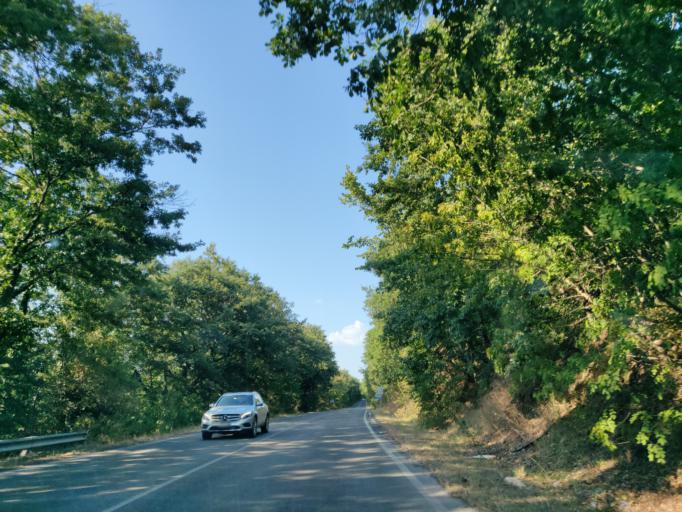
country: IT
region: Latium
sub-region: Provincia di Viterbo
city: Valentano
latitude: 42.5951
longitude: 11.8380
